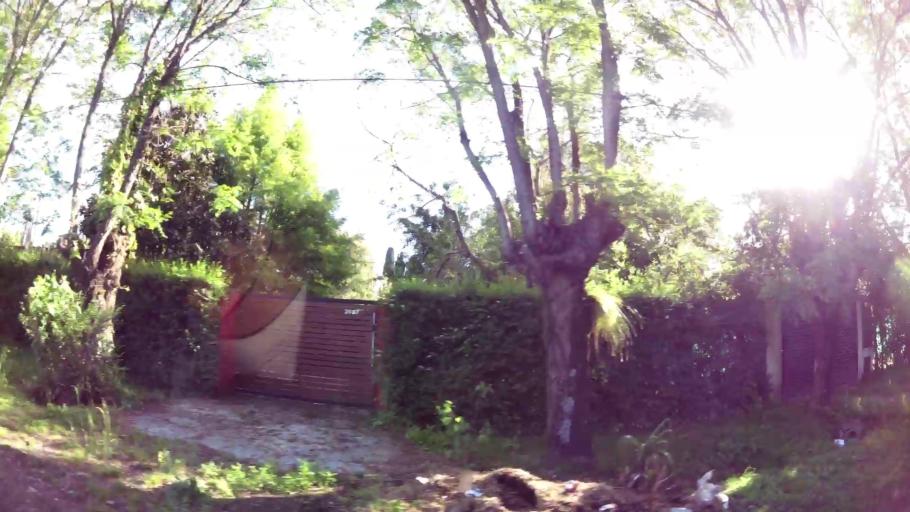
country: AR
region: Buenos Aires
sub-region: Partido de Quilmes
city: Quilmes
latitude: -34.8160
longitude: -58.2152
